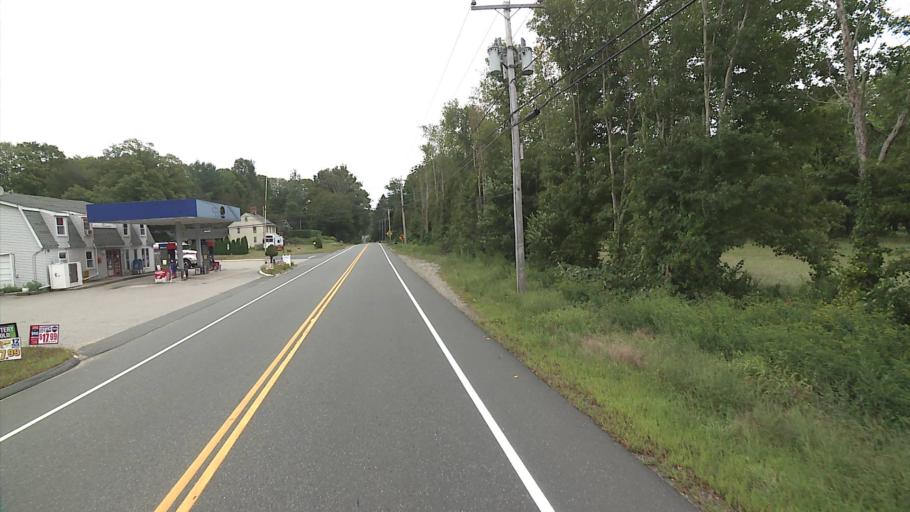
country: US
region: Connecticut
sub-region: New London County
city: Colchester
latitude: 41.5017
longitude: -72.2854
